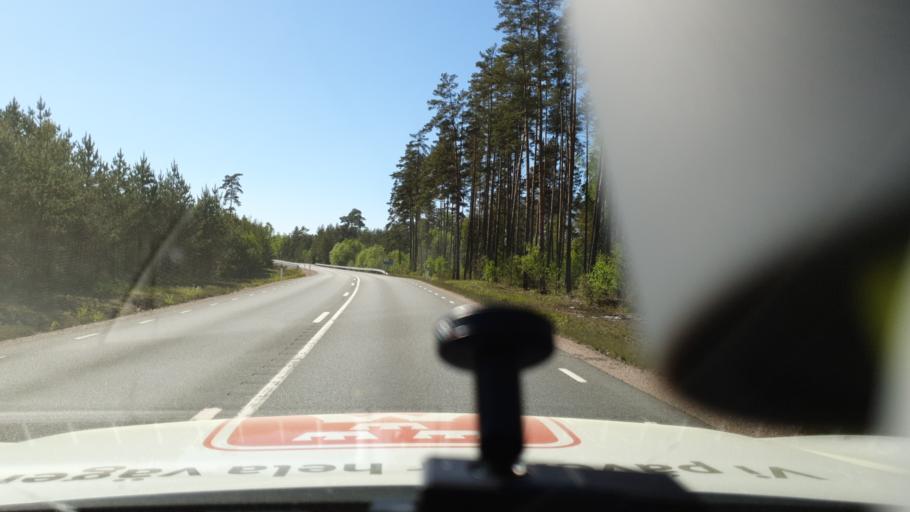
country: SE
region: Kalmar
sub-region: Hultsfreds Kommun
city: Virserum
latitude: 57.3988
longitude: 15.4236
